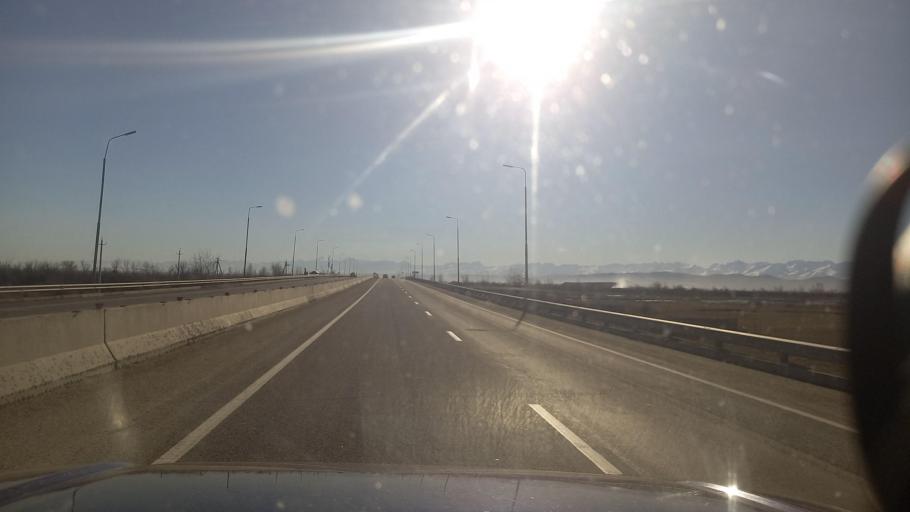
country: RU
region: Kabardino-Balkariya
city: Kishpek
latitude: 43.6035
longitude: 43.6608
